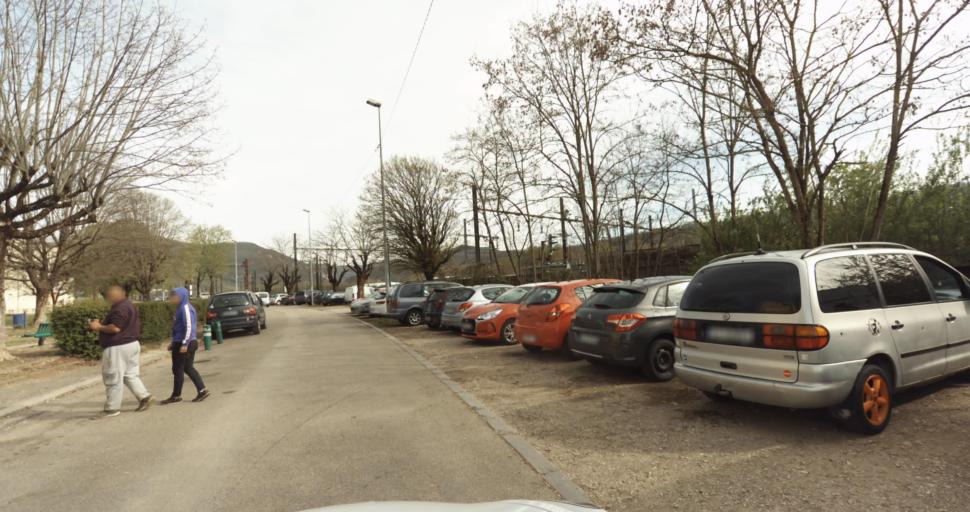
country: FR
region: Rhone-Alpes
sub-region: Departement de l'Ain
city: Amberieu-en-Bugey
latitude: 45.9540
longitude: 5.3448
